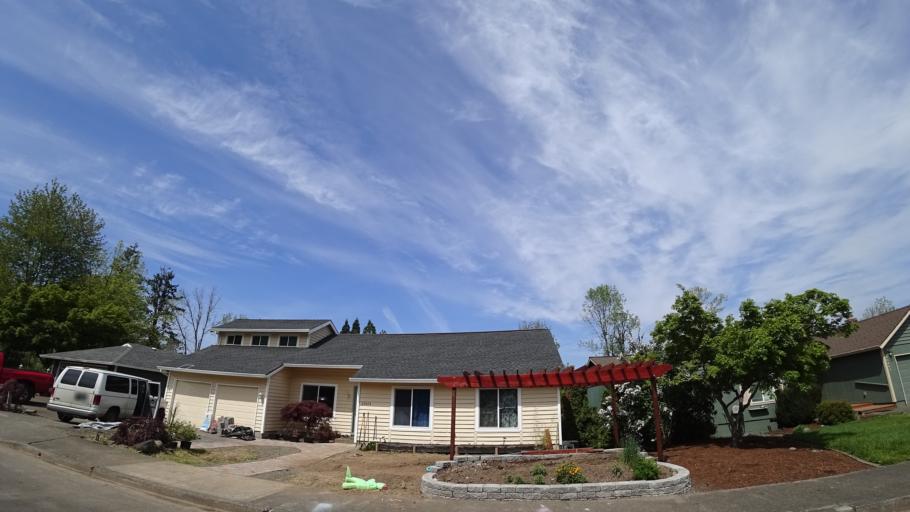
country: US
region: Oregon
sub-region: Washington County
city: Aloha
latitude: 45.4832
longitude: -122.8875
